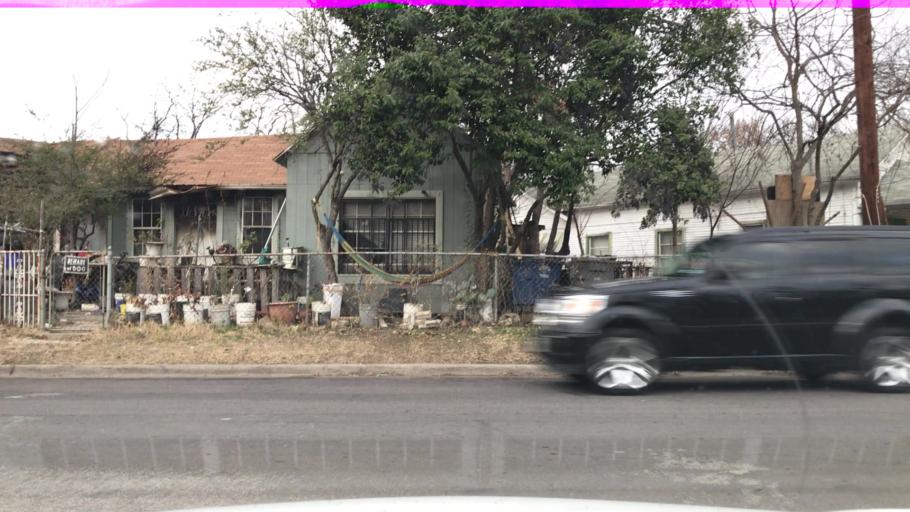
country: US
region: Texas
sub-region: Dallas County
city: Dallas
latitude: 32.7513
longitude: -96.7560
